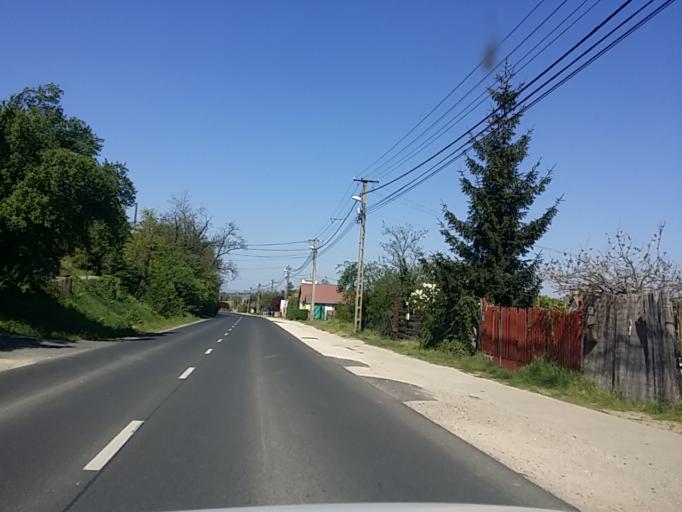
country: HU
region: Pest
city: Mogyorod
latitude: 47.5985
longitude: 19.2607
